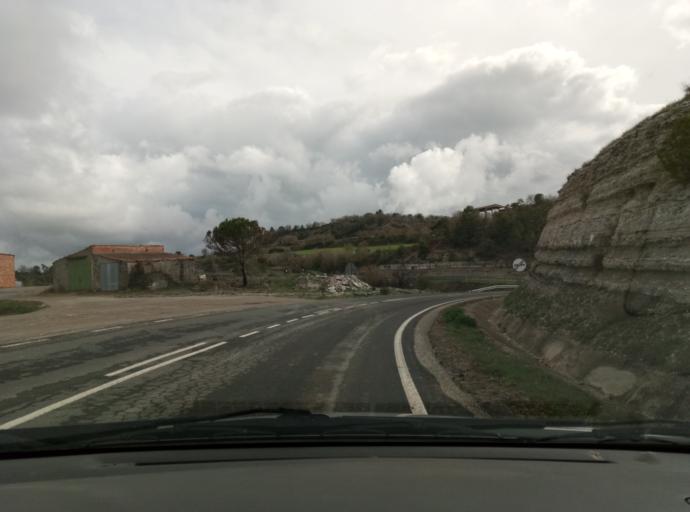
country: ES
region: Catalonia
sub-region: Provincia de Tarragona
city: Santa Coloma de Queralt
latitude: 41.5783
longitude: 1.3364
